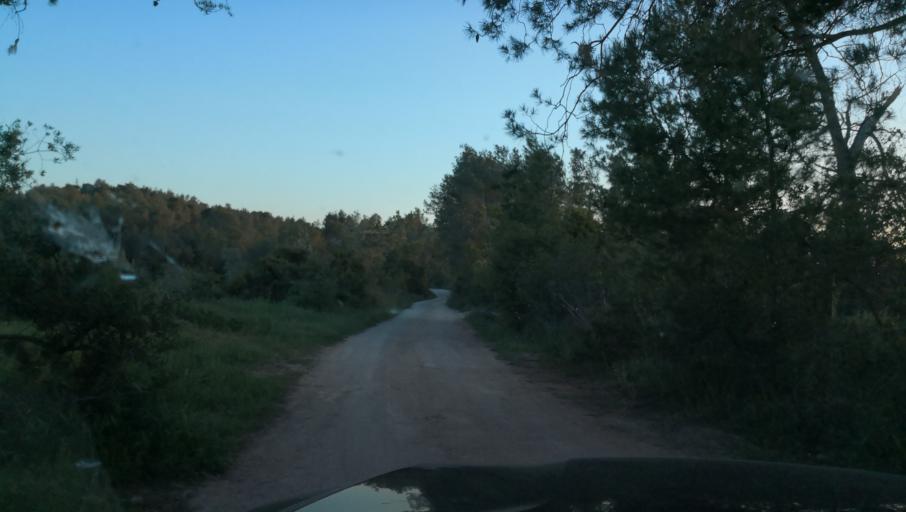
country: PT
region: Setubal
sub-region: Setubal
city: Setubal
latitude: 38.5235
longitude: -8.9183
